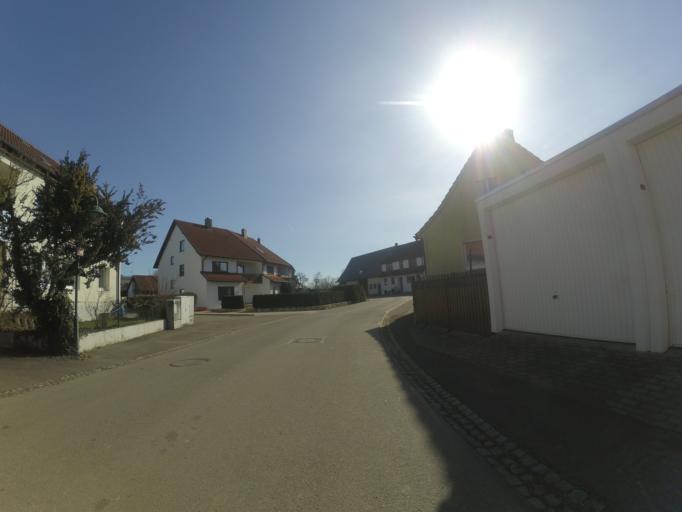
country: DE
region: Baden-Wuerttemberg
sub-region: Tuebingen Region
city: Langenau
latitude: 48.5018
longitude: 10.1409
